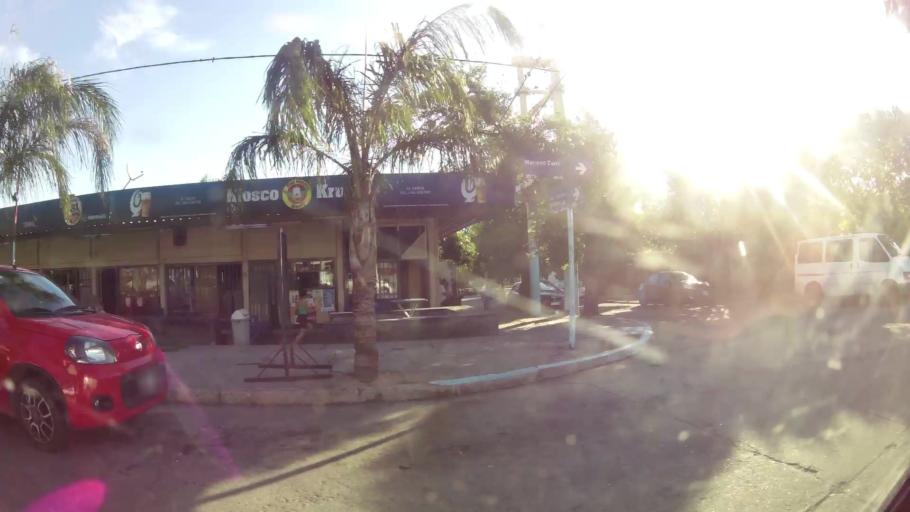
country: AR
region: Cordoba
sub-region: Departamento de Capital
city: Cordoba
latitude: -31.3792
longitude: -64.2379
